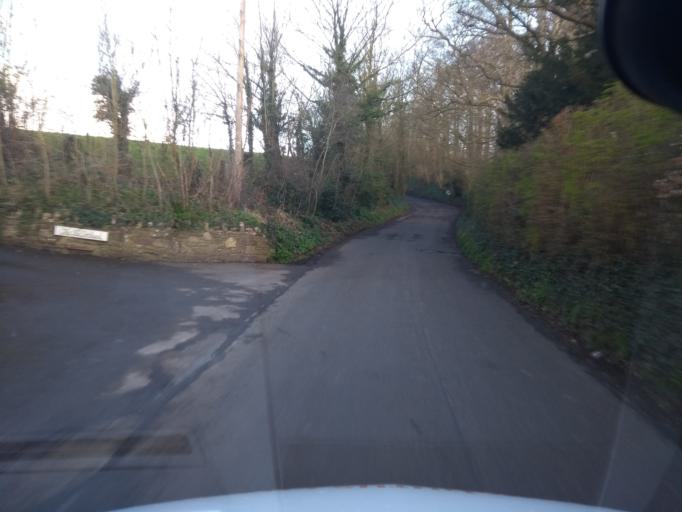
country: GB
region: England
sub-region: Somerset
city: Wedmore
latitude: 51.2285
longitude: -2.8135
